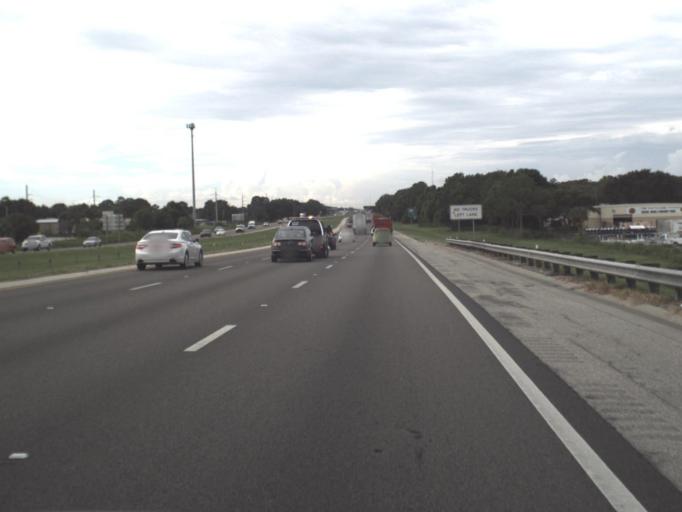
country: US
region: Florida
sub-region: Sarasota County
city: Fruitville
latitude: 27.3247
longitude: -82.4480
